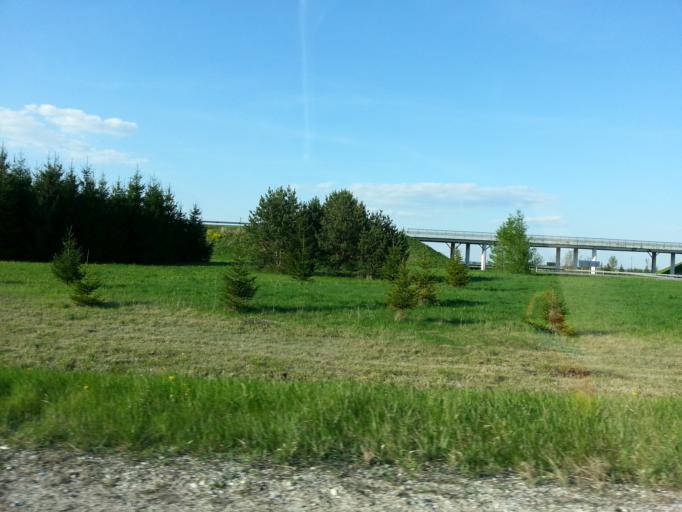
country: LT
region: Vilnius County
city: Ukmerge
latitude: 55.3967
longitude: 24.6997
